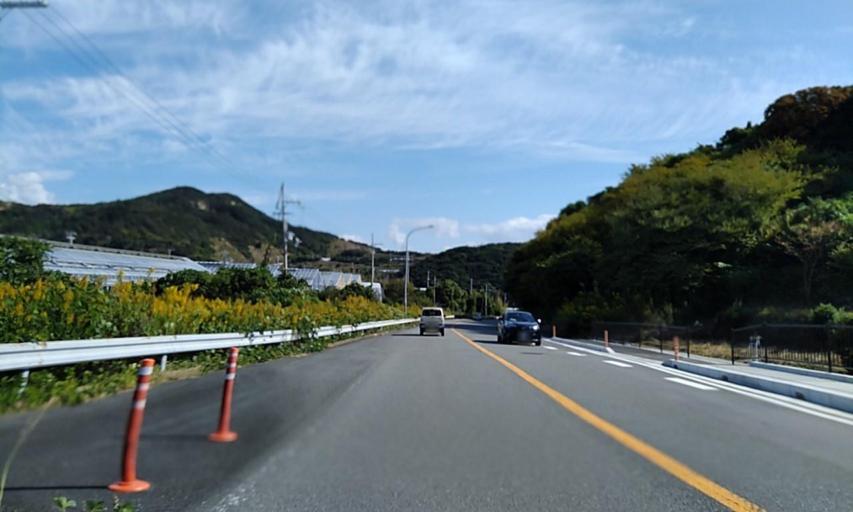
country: JP
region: Wakayama
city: Gobo
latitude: 33.8441
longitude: 135.1729
